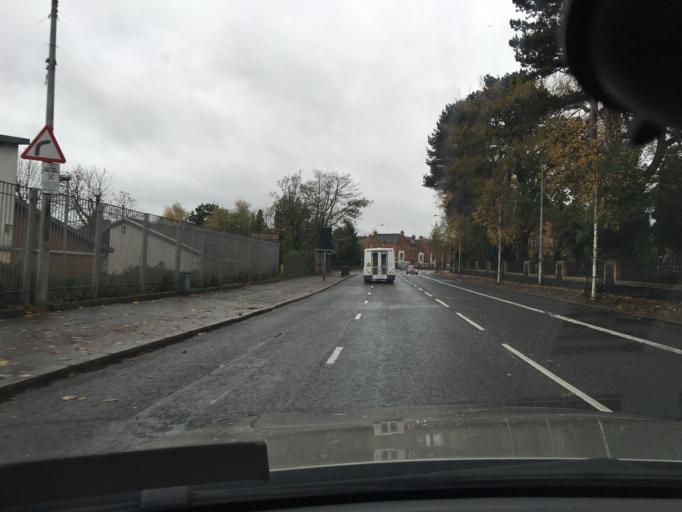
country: GB
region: Northern Ireland
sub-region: City of Belfast
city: Belfast
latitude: 54.5873
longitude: -5.9713
